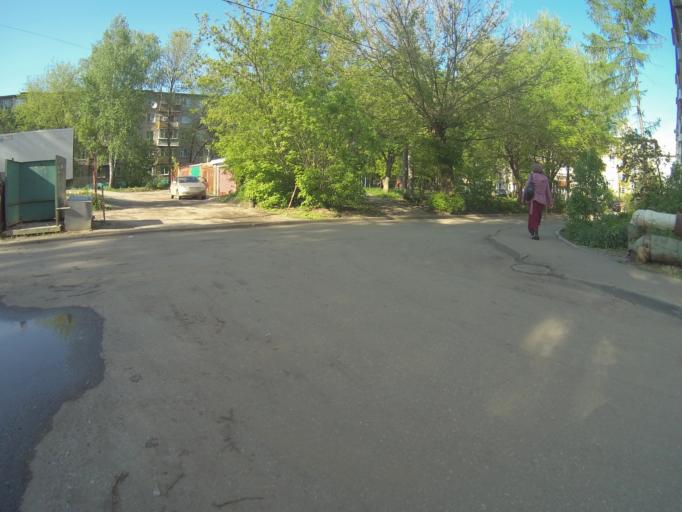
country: RU
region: Vladimir
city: Bogolyubovo
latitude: 56.1718
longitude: 40.4764
